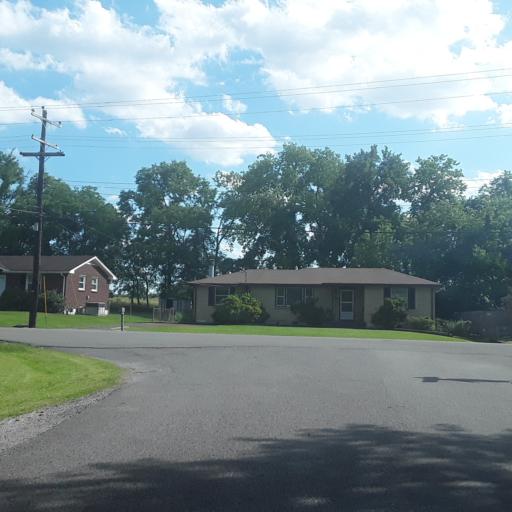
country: US
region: Tennessee
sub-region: Davidson County
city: Lakewood
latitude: 36.2036
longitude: -86.6353
